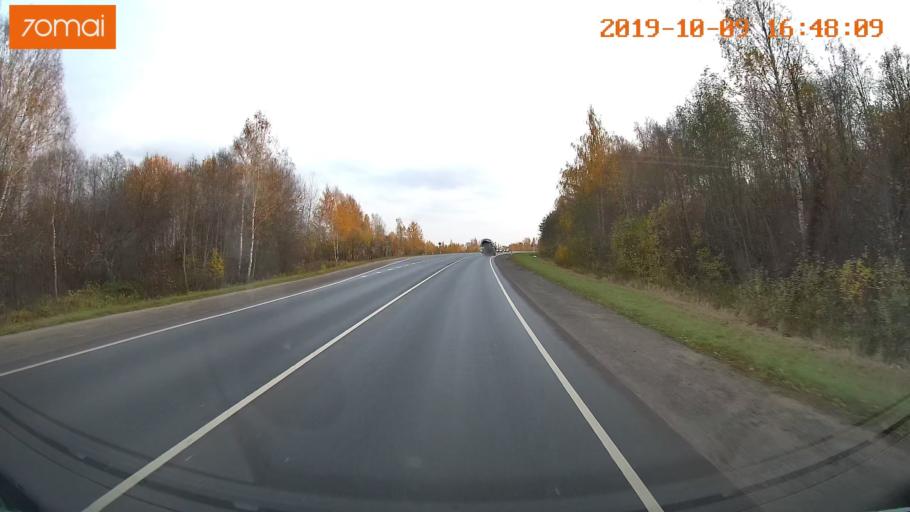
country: RU
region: Kostroma
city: Volgorechensk
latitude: 57.4310
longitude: 41.1888
